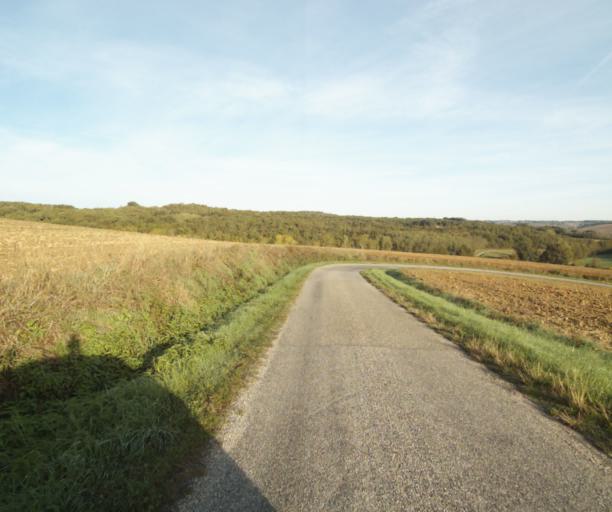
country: FR
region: Midi-Pyrenees
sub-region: Departement du Tarn-et-Garonne
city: Nohic
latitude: 43.9230
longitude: 1.4813
